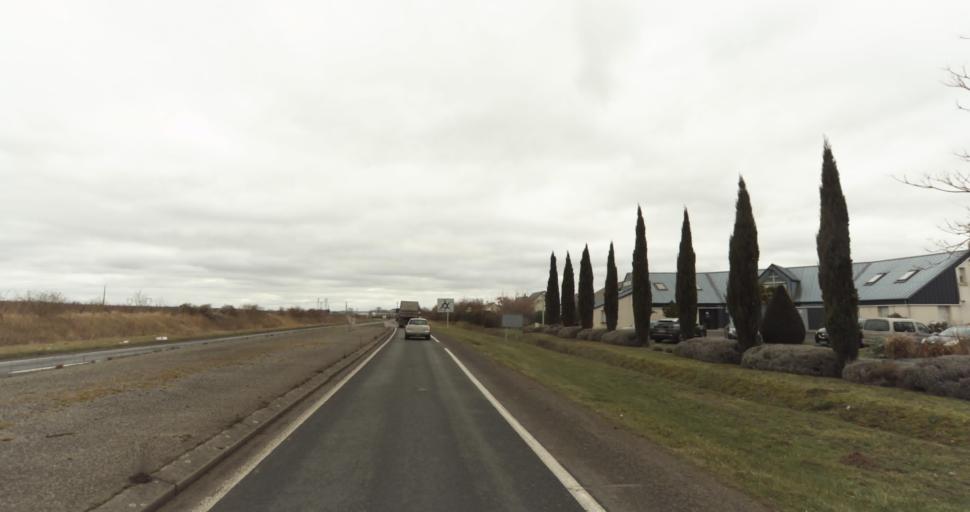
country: FR
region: Pays de la Loire
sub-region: Departement de Maine-et-Loire
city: Varrains
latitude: 47.2167
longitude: -0.0597
